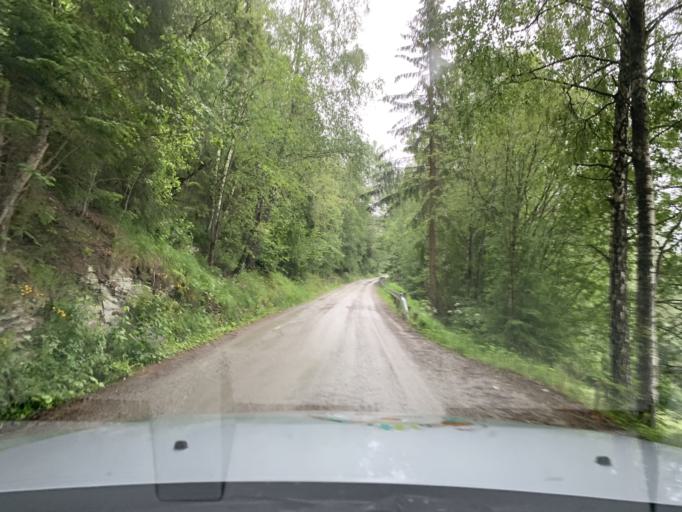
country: NO
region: Oppland
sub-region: Oyer
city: Tretten
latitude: 61.3913
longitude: 10.2581
